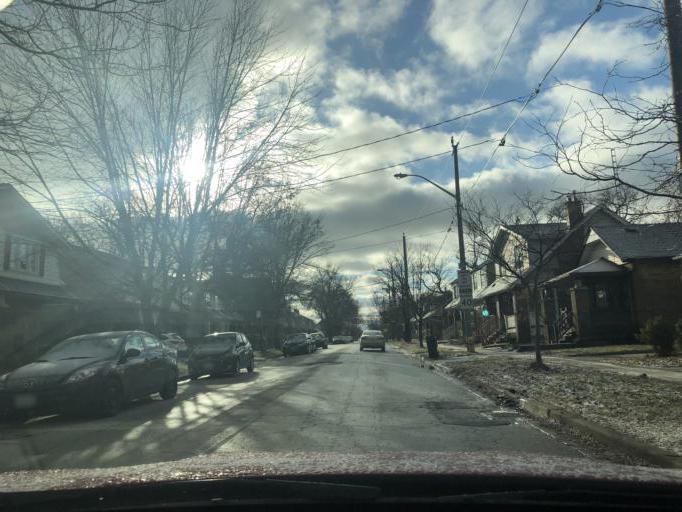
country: CA
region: Ontario
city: Toronto
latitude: 43.6856
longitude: -79.3341
